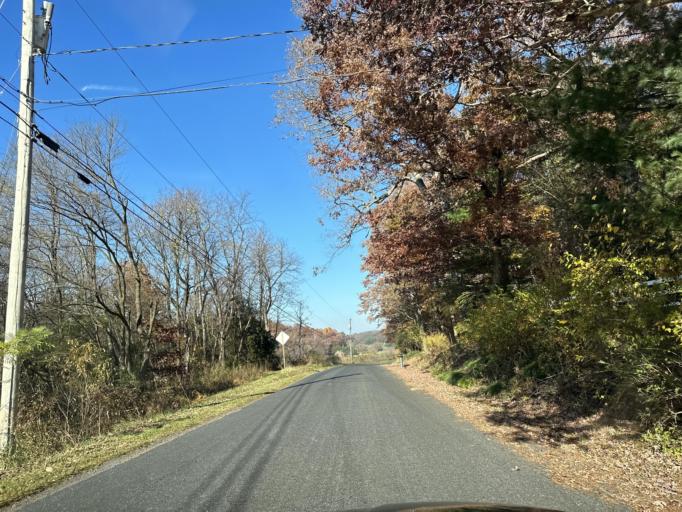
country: US
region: Virginia
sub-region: Augusta County
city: Weyers Cave
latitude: 38.2953
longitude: -78.9224
